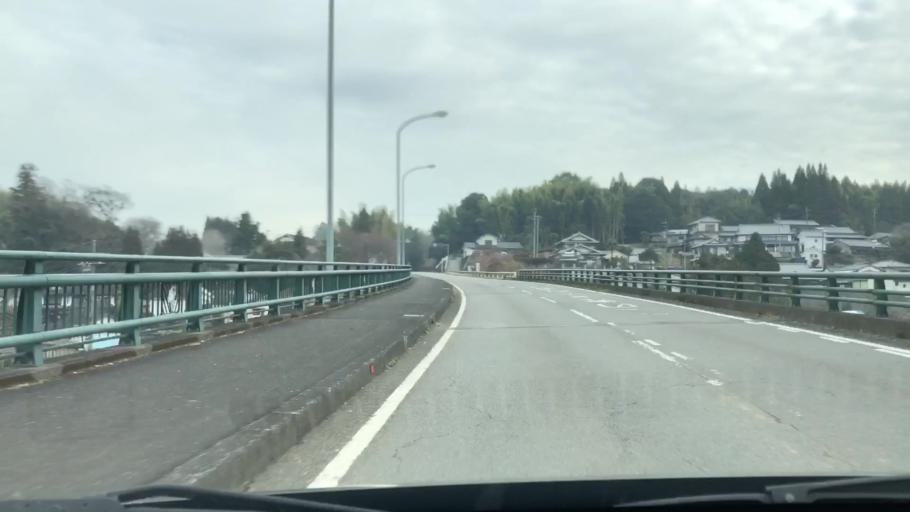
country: JP
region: Oita
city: Usuki
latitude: 33.0142
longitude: 131.6661
